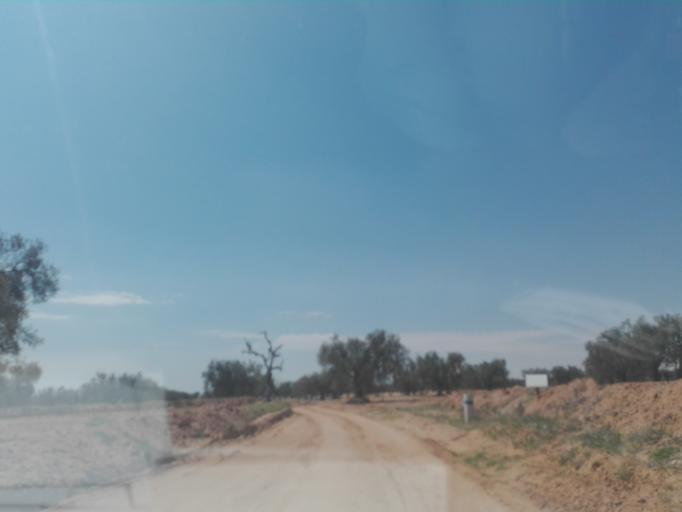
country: TN
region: Safaqis
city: Bi'r `Ali Bin Khalifah
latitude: 34.6081
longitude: 10.3528
